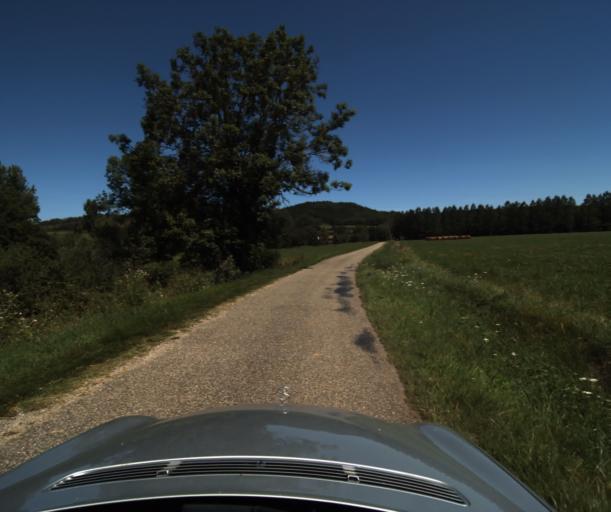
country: FR
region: Languedoc-Roussillon
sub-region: Departement de l'Aude
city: Chalabre
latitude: 42.9949
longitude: 1.9259
